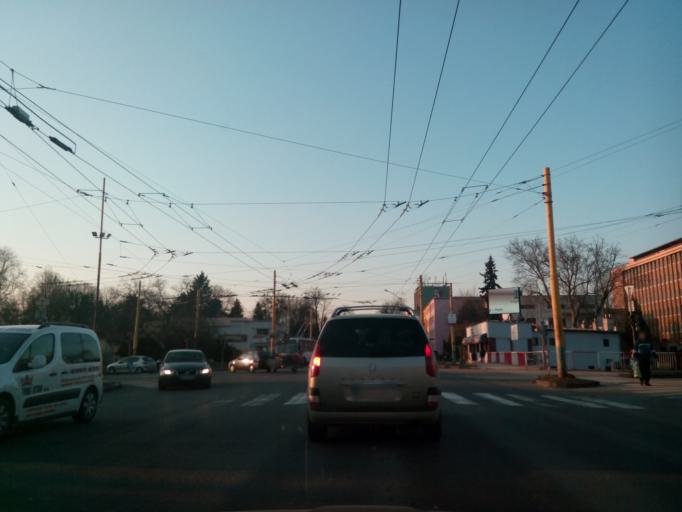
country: SK
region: Presovsky
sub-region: Okres Presov
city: Presov
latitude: 48.9882
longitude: 21.2479
